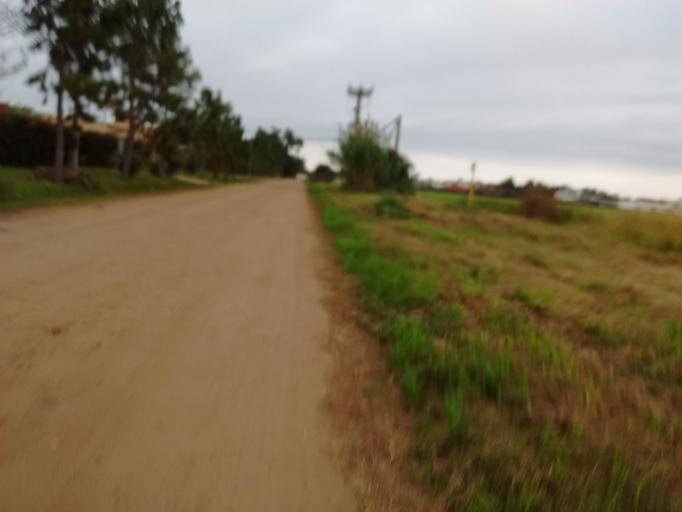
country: AR
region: Santa Fe
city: Funes
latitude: -32.9340
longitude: -60.8286
